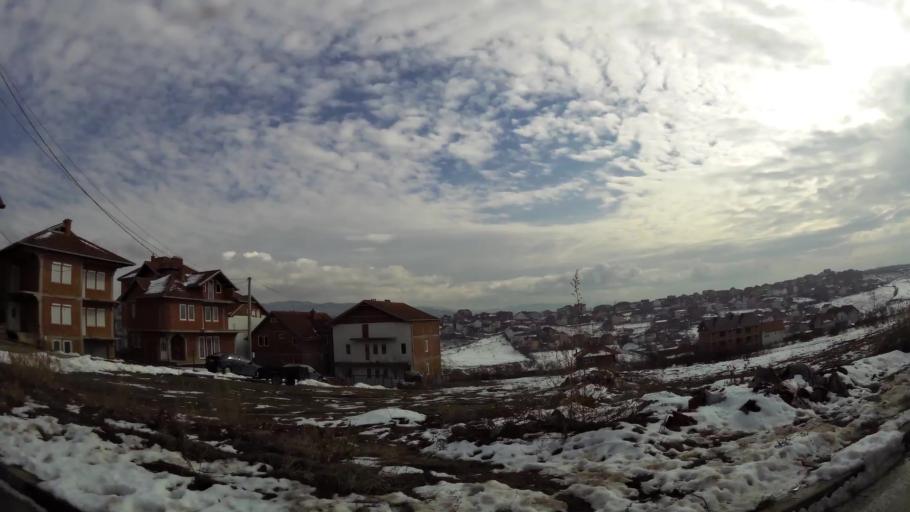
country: XK
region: Pristina
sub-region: Komuna e Prishtines
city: Pristina
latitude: 42.6820
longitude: 21.1528
